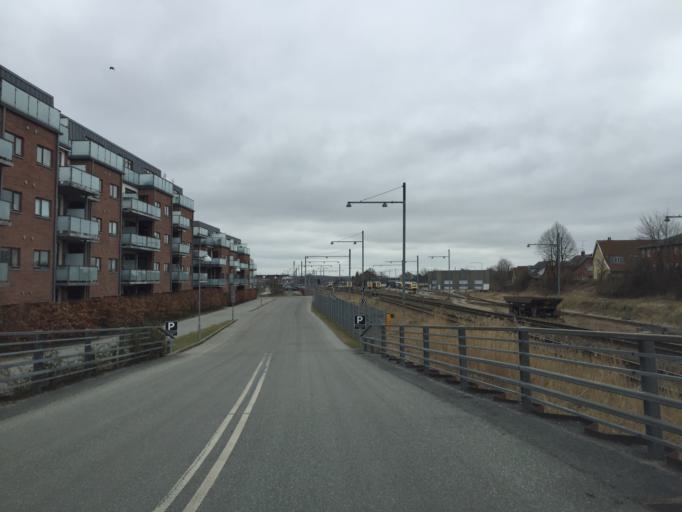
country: DK
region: Capital Region
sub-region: Hillerod Kommune
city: Hillerod
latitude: 55.9322
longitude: 12.3130
